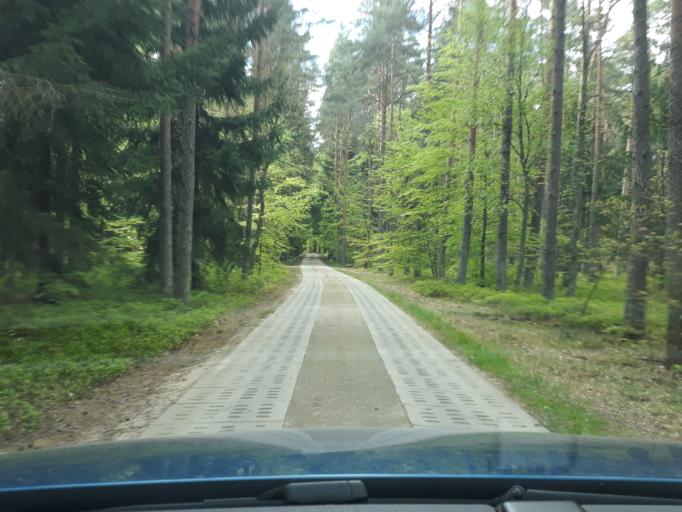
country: PL
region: Pomeranian Voivodeship
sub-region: Powiat czluchowski
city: Czluchow
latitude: 53.7447
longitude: 17.3394
